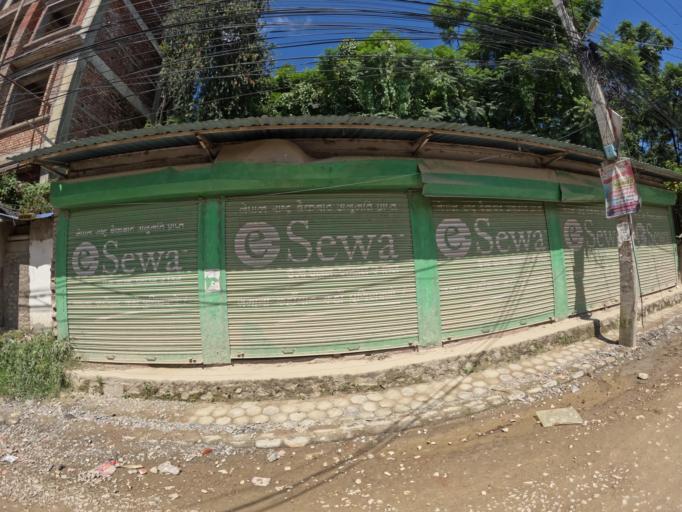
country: NP
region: Central Region
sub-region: Bagmati Zone
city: Kathmandu
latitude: 27.7399
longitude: 85.3258
